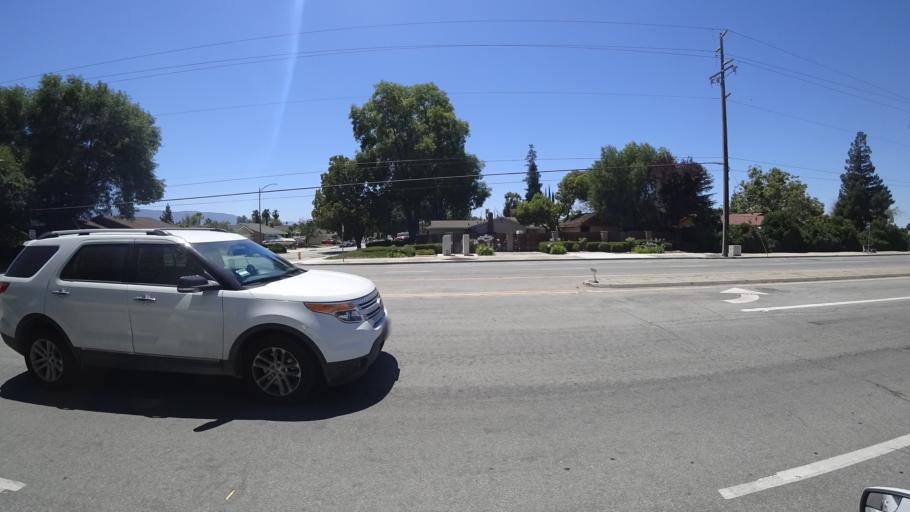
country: US
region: California
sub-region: Santa Clara County
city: Seven Trees
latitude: 37.2579
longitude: -121.8307
